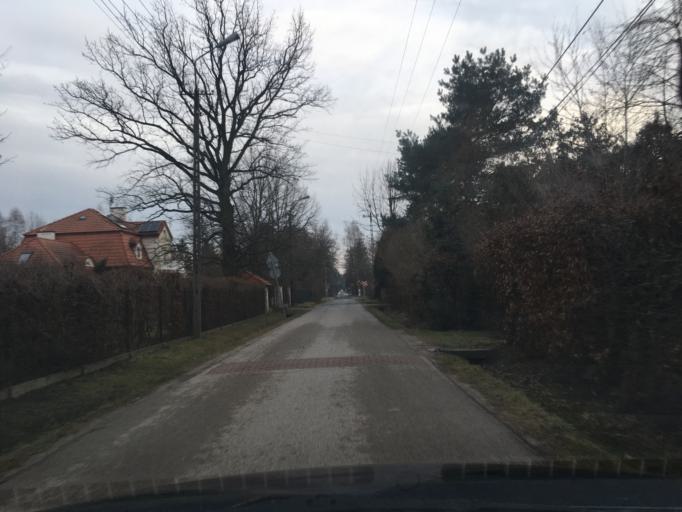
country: PL
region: Masovian Voivodeship
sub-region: Powiat piaseczynski
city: Lesznowola
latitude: 52.0355
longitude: 20.9579
